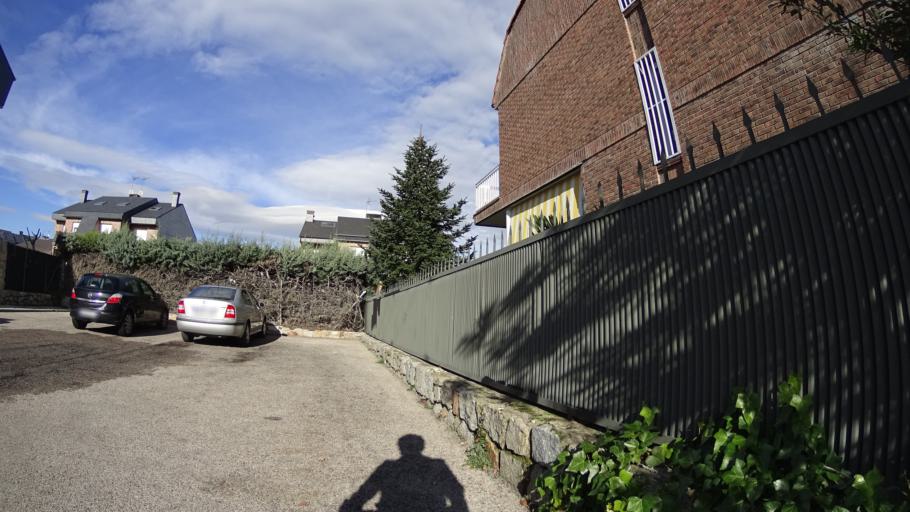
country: ES
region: Madrid
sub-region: Provincia de Madrid
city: Galapagar
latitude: 40.5784
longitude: -4.0115
